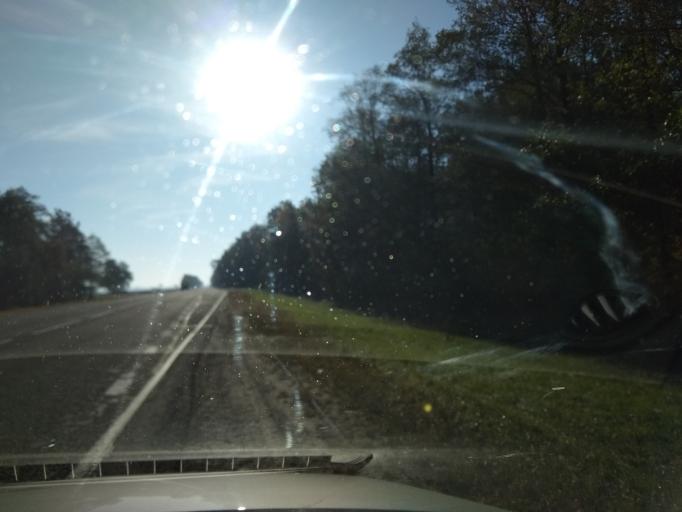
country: BY
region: Brest
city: Malaryta
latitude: 51.8731
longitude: 24.1777
